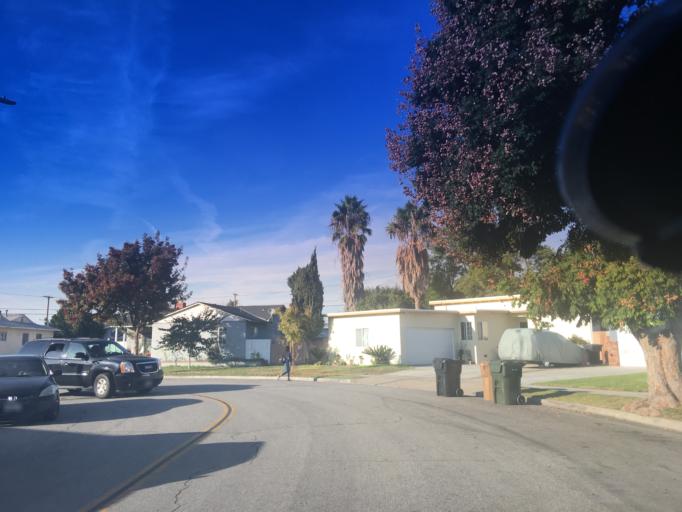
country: US
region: California
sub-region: Orange County
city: Anaheim
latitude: 33.8255
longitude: -117.8938
